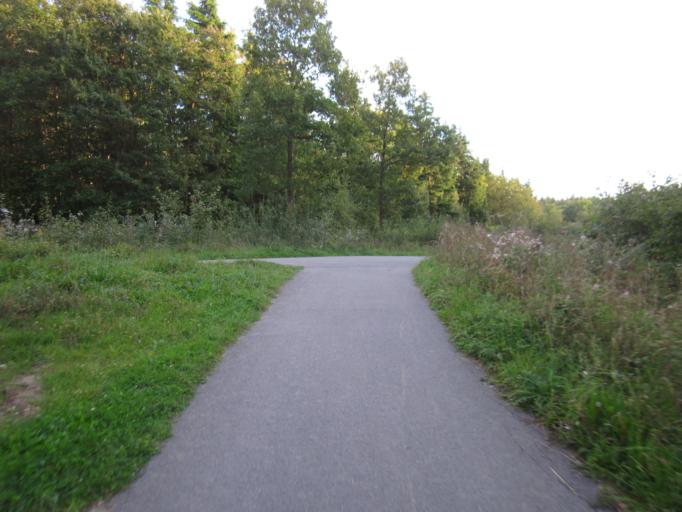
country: GB
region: England
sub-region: Kent
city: Blean
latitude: 51.3319
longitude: 1.0492
